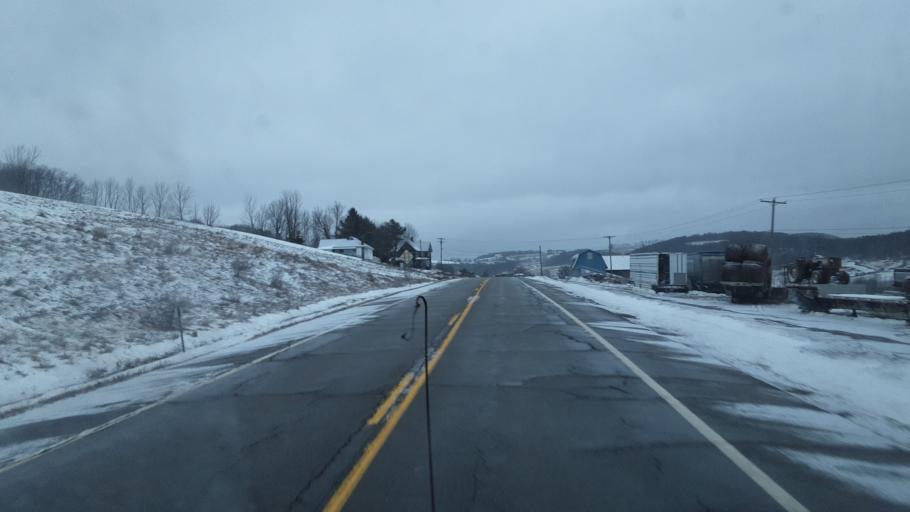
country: US
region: New York
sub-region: Steuben County
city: Canisteo
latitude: 42.1376
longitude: -77.5169
